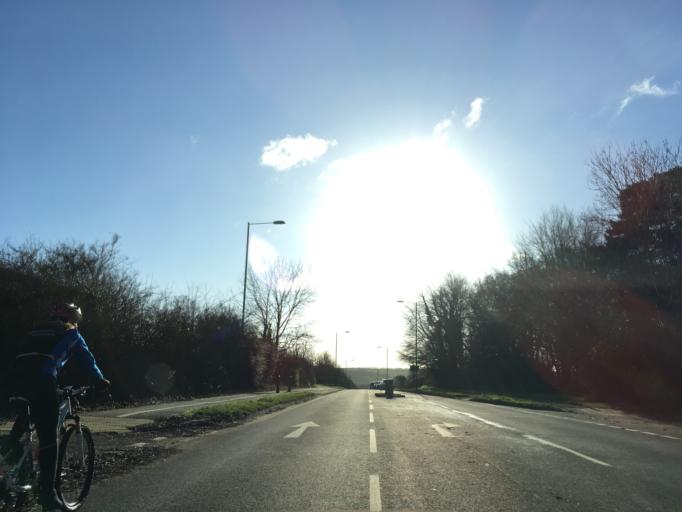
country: GB
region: England
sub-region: Borough of Swindon
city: Swindon
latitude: 51.5432
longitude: -1.7709
